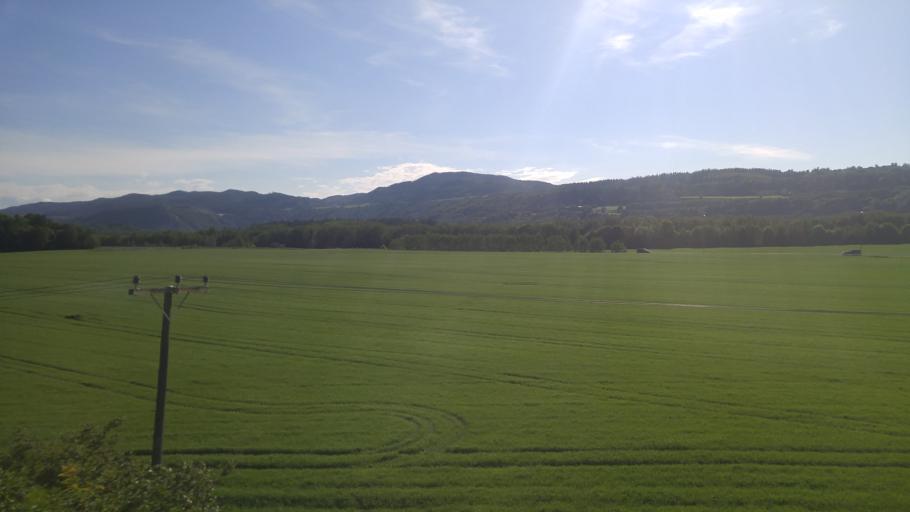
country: NO
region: Sor-Trondelag
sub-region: Melhus
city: Melhus
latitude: 63.2736
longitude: 10.2909
